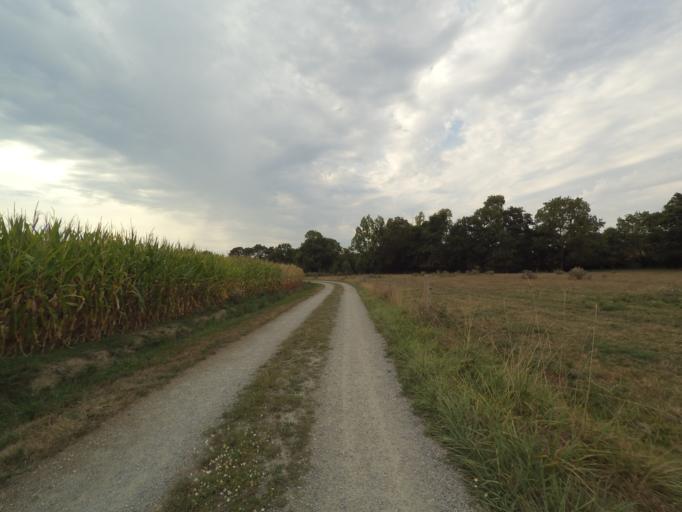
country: FR
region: Pays de la Loire
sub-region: Departement de la Vendee
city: Bouffere
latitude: 46.9850
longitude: -1.3703
